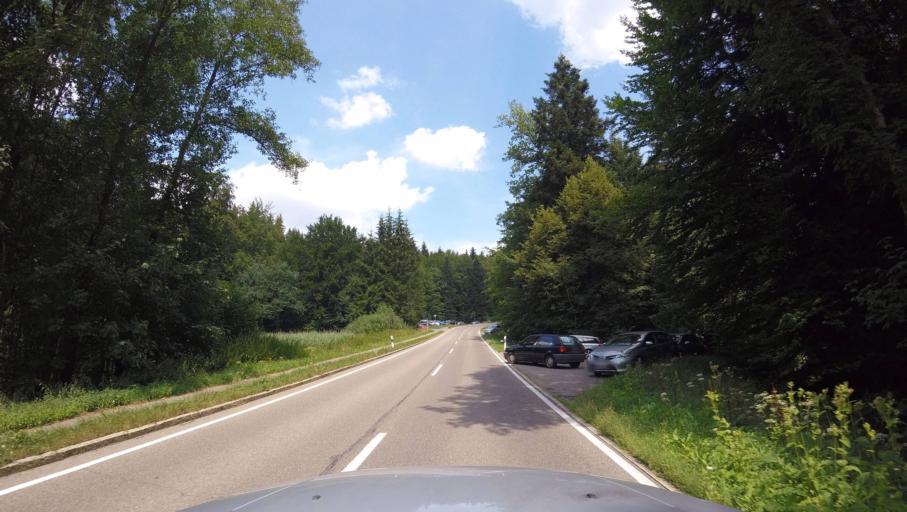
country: DE
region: Baden-Wuerttemberg
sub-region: Regierungsbezirk Stuttgart
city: Kaisersbach
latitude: 48.9221
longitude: 9.6152
